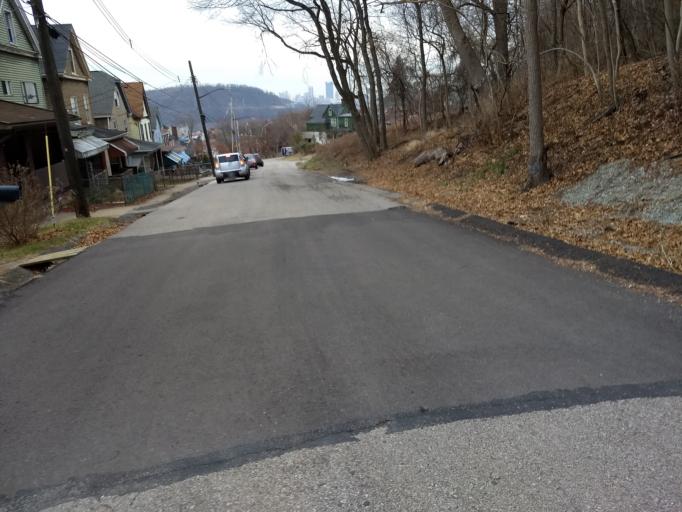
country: US
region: Pennsylvania
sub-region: Allegheny County
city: Homestead
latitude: 40.4074
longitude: -79.9368
